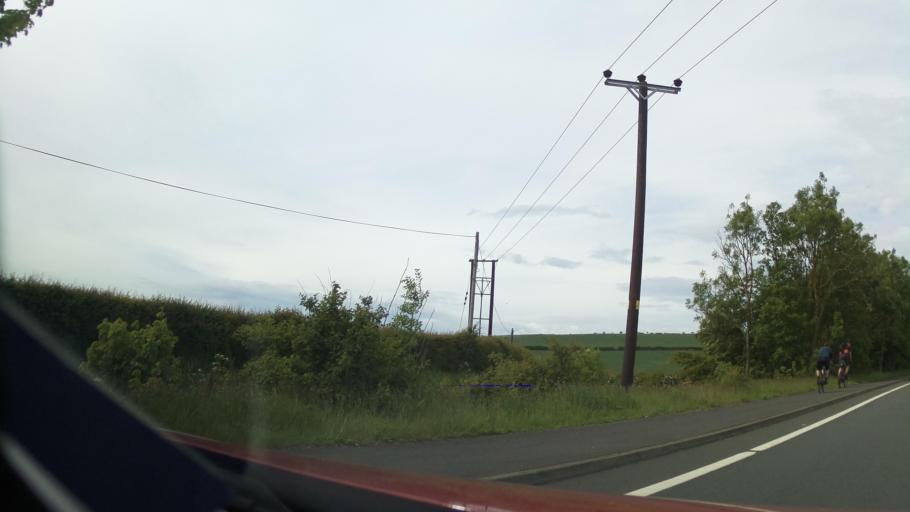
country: GB
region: England
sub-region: Northumberland
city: Berwick-Upon-Tweed
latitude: 55.7706
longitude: -2.0436
